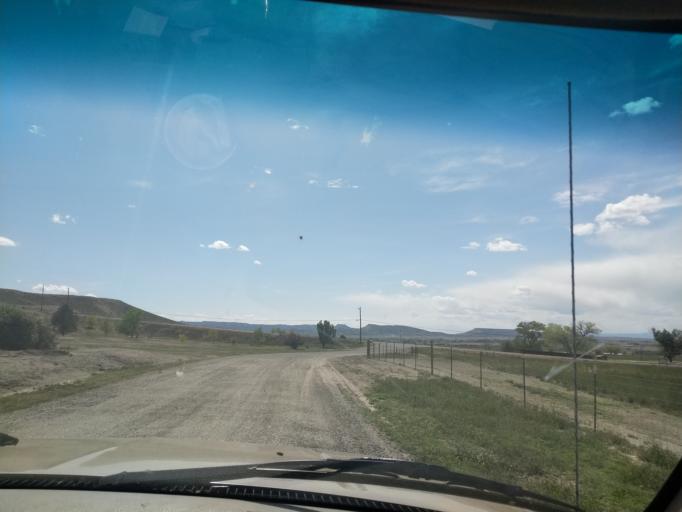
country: US
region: Colorado
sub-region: Mesa County
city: Fruita
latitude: 39.2102
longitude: -108.7554
